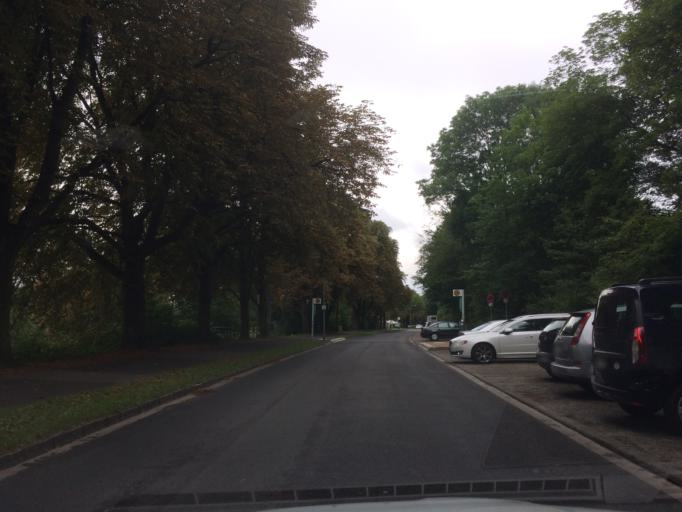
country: DE
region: Hesse
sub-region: Regierungsbezirk Kassel
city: Kassel
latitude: 51.3062
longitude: 9.5016
